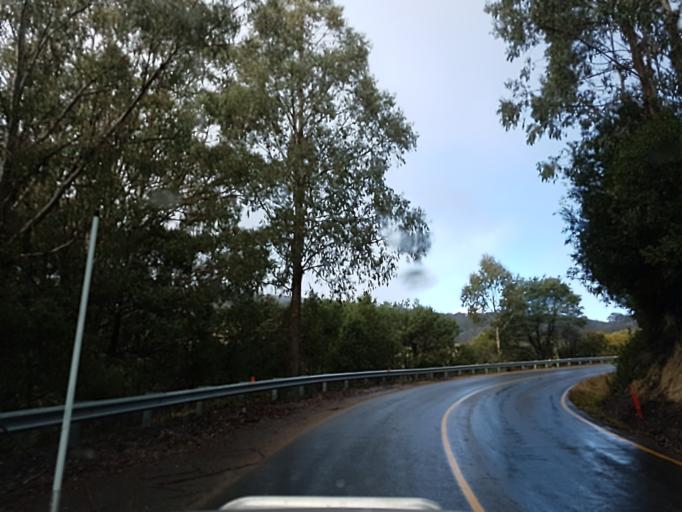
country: AU
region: Victoria
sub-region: Yarra Ranges
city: Millgrove
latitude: -37.5245
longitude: 145.8659
